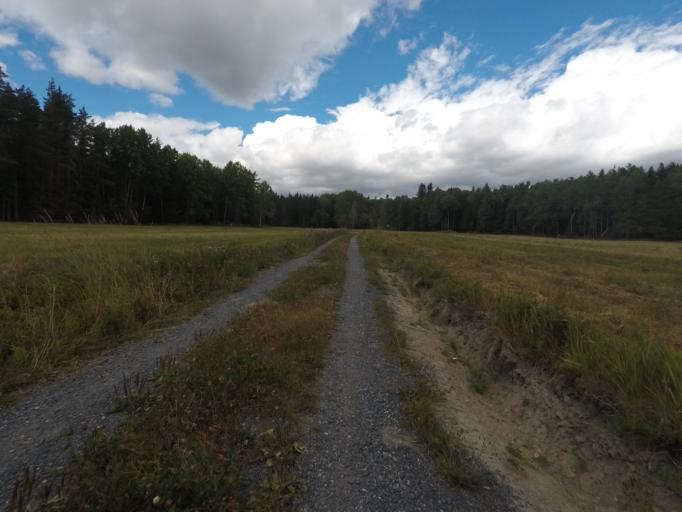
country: SE
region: Soedermanland
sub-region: Eskilstuna Kommun
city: Kvicksund
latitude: 59.3999
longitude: 16.3062
